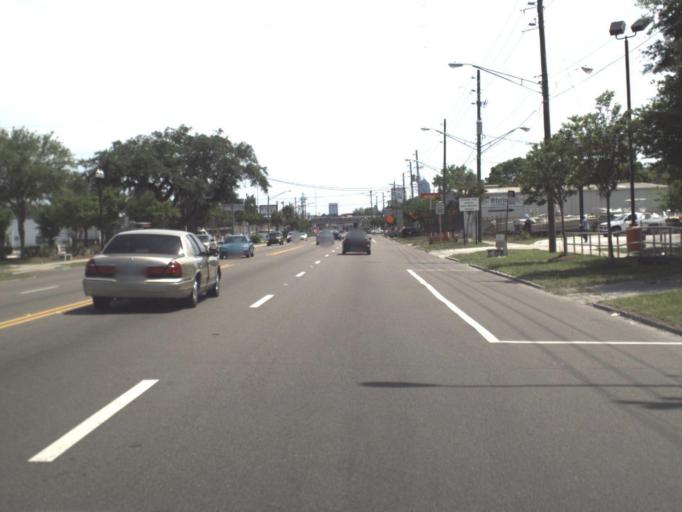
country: US
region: Florida
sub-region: Duval County
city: Jacksonville
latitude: 30.3604
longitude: -81.6536
